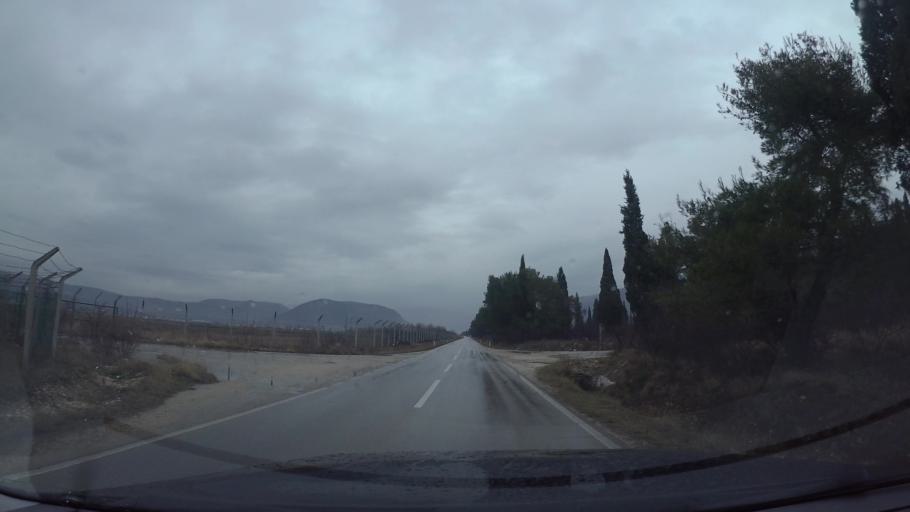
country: BA
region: Federation of Bosnia and Herzegovina
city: Rodoc
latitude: 43.2919
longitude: 17.8464
